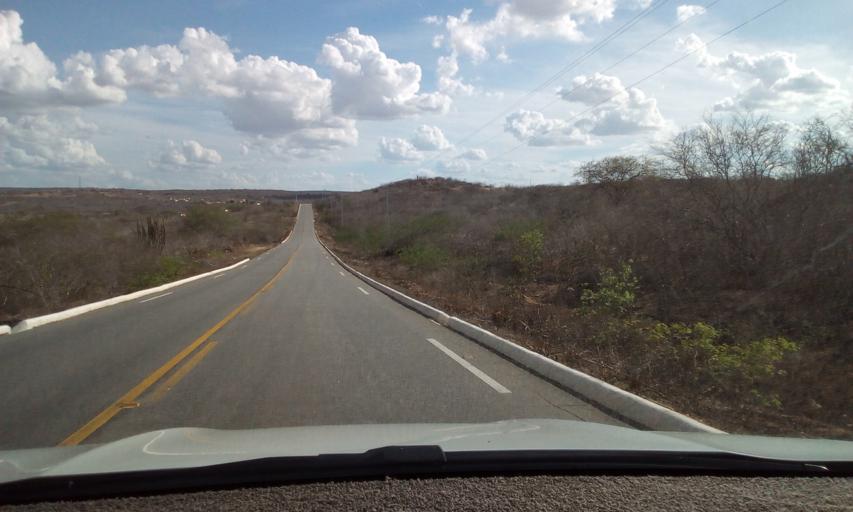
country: BR
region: Paraiba
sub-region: Soledade
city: Soledade
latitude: -6.8447
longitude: -36.4074
